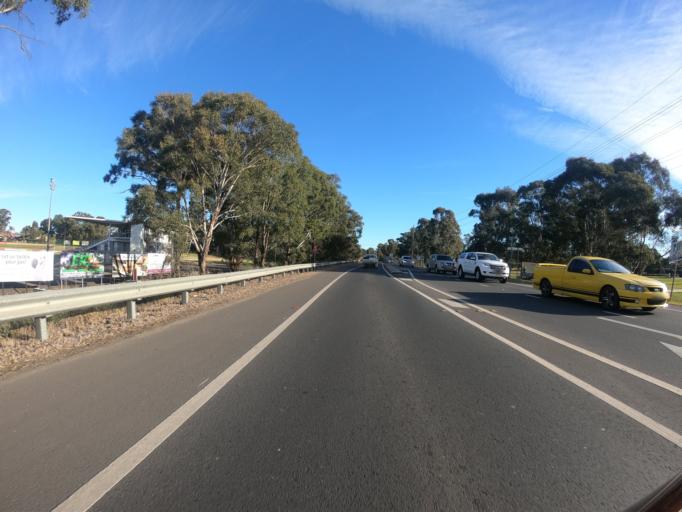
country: AU
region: New South Wales
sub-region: Hawkesbury
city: South Windsor
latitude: -33.6307
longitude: 150.7928
